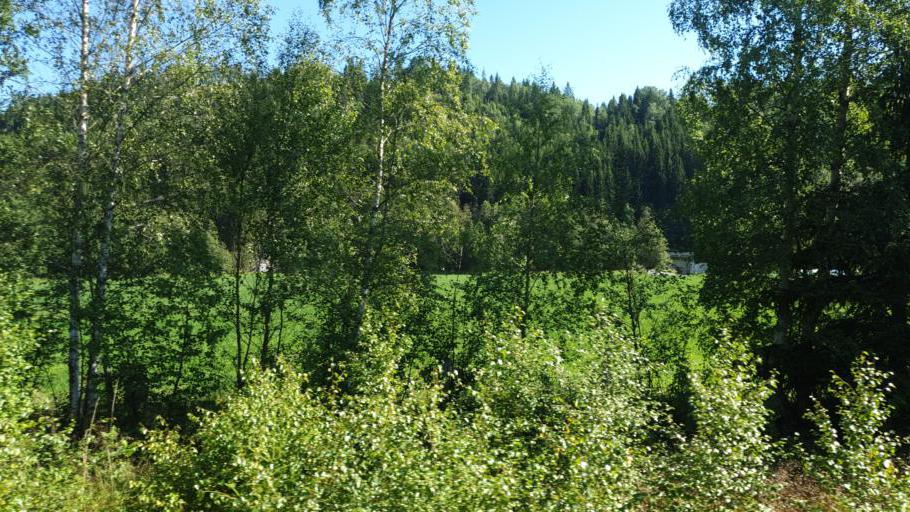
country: NO
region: Sor-Trondelag
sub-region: Meldal
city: Meldal
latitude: 63.1795
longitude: 9.7627
